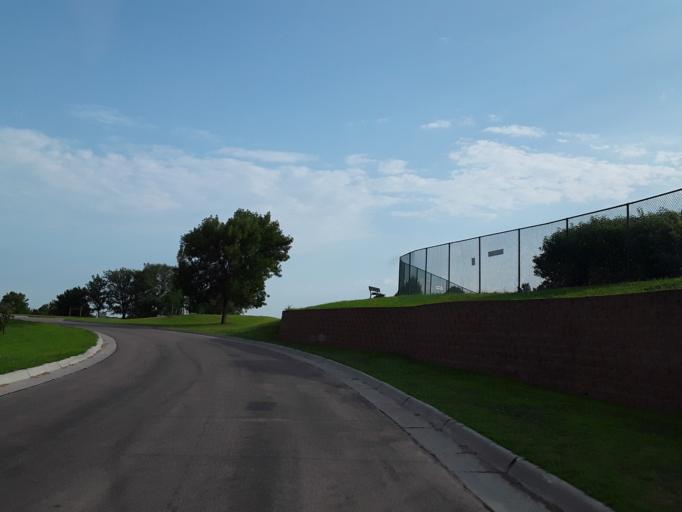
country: US
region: Nebraska
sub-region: Saunders County
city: Ashland
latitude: 41.0263
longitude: -96.3096
